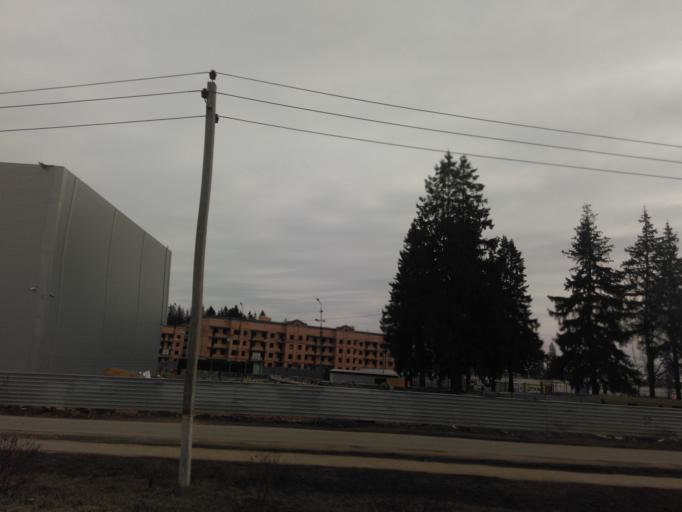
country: RU
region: Moskovskaya
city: Tuchkovo
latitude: 55.6049
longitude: 36.4903
